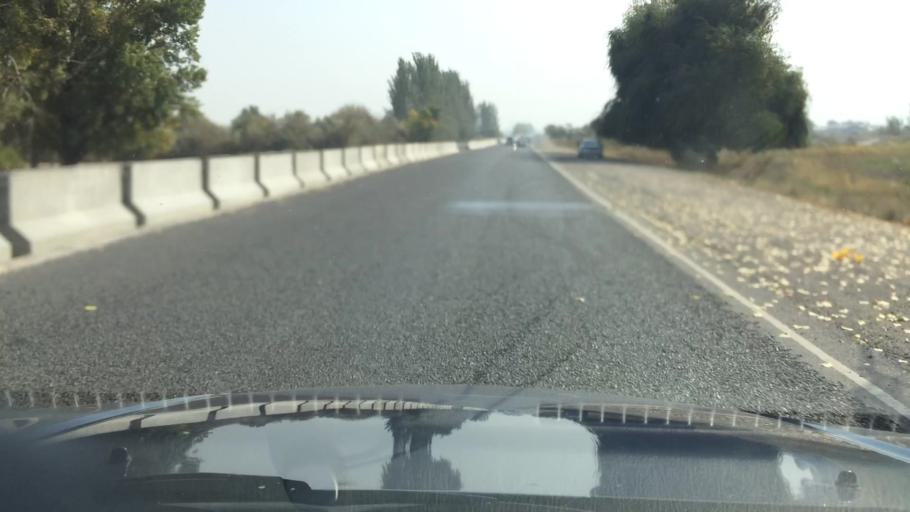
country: KG
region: Chuy
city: Kant
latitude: 42.9744
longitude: 74.8951
